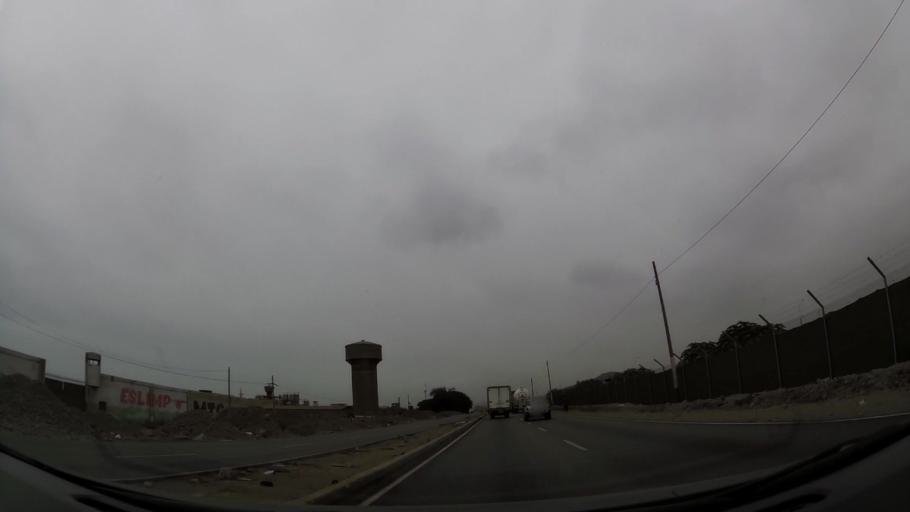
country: PE
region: Callao
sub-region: Callao
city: Callao
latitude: -12.0069
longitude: -77.1276
